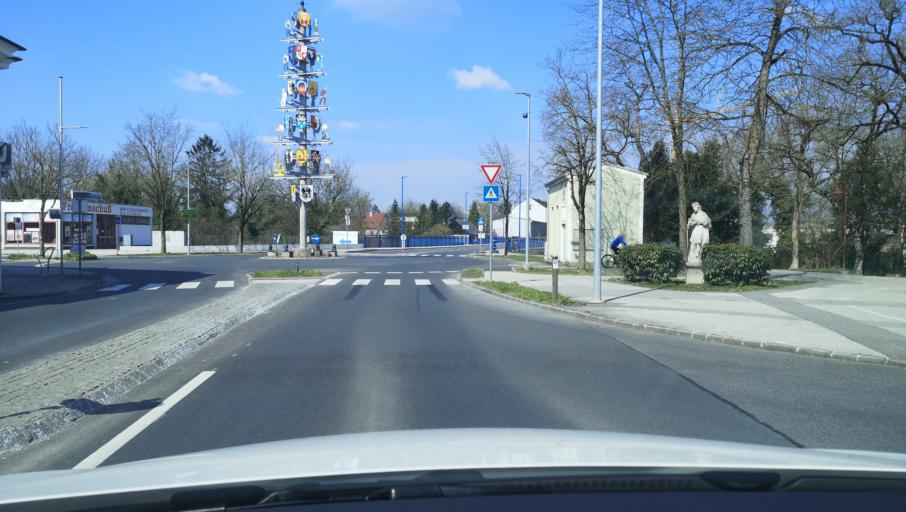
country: AT
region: Lower Austria
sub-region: Politischer Bezirk Amstetten
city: Winklarn
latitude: 48.0769
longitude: 14.8157
